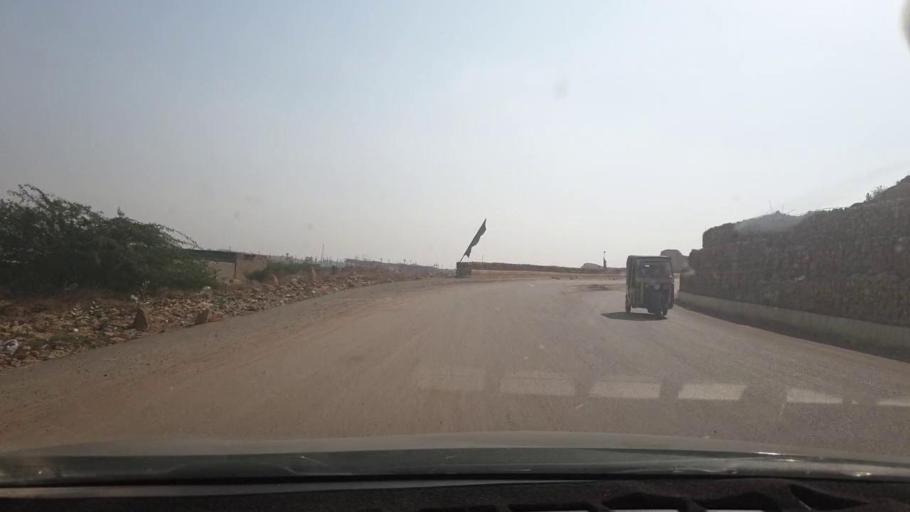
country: PK
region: Sindh
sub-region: Karachi District
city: Karachi
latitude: 24.9732
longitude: 66.9981
